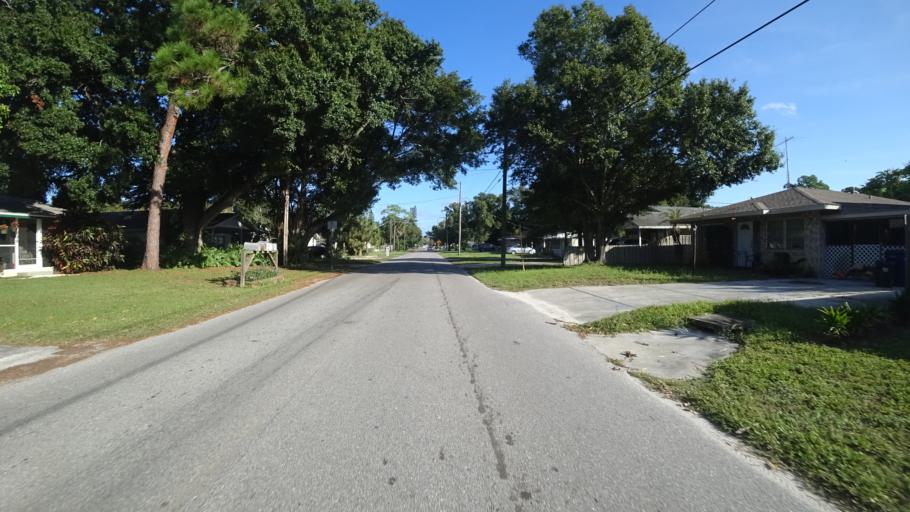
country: US
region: Florida
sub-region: Manatee County
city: West Bradenton
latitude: 27.4888
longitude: -82.5998
